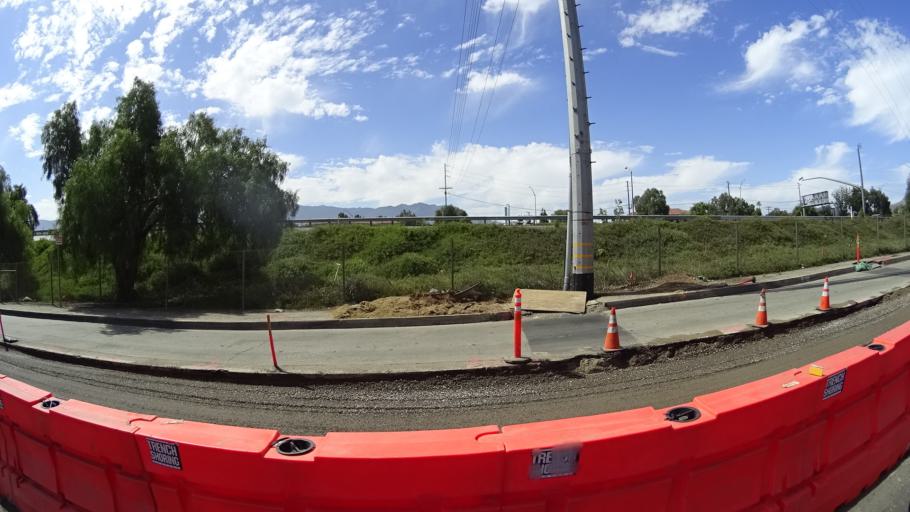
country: US
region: California
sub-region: Ventura County
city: Casa Conejo
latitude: 34.1911
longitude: -118.9403
